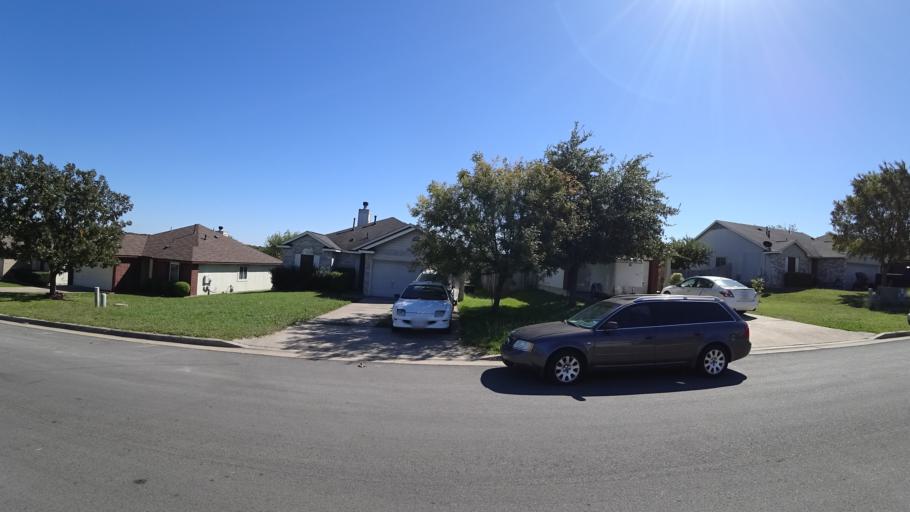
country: US
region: Texas
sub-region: Travis County
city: Hornsby Bend
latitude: 30.3054
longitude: -97.6404
